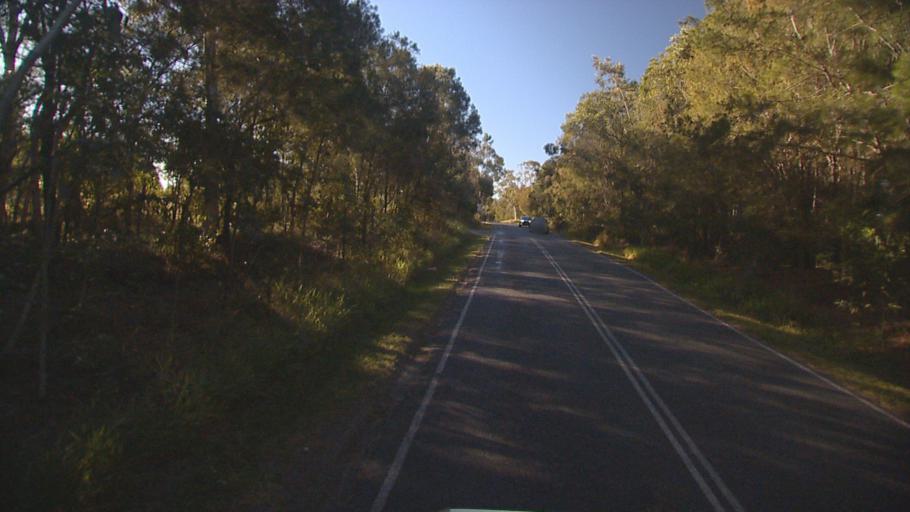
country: AU
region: Queensland
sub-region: Logan
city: Logan Reserve
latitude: -27.7272
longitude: 153.0899
